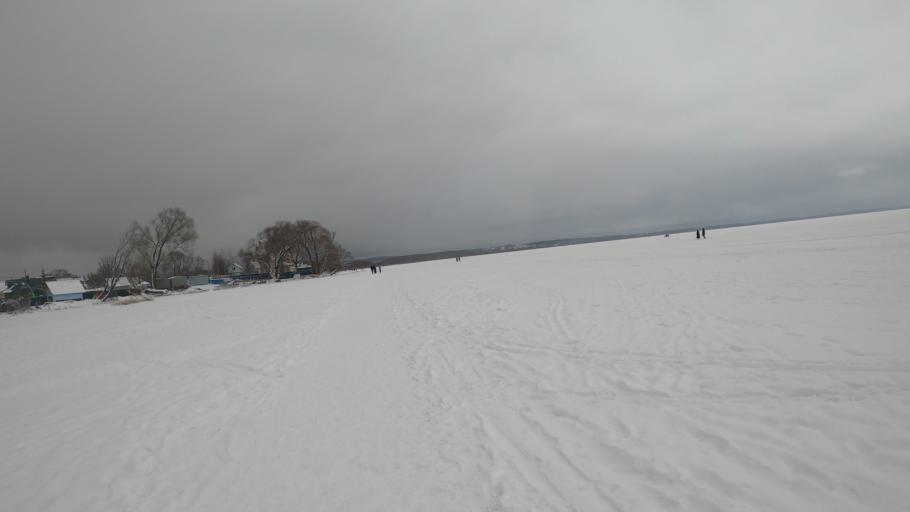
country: RU
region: Jaroslavl
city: Pereslavl'-Zalesskiy
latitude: 56.7368
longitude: 38.8300
